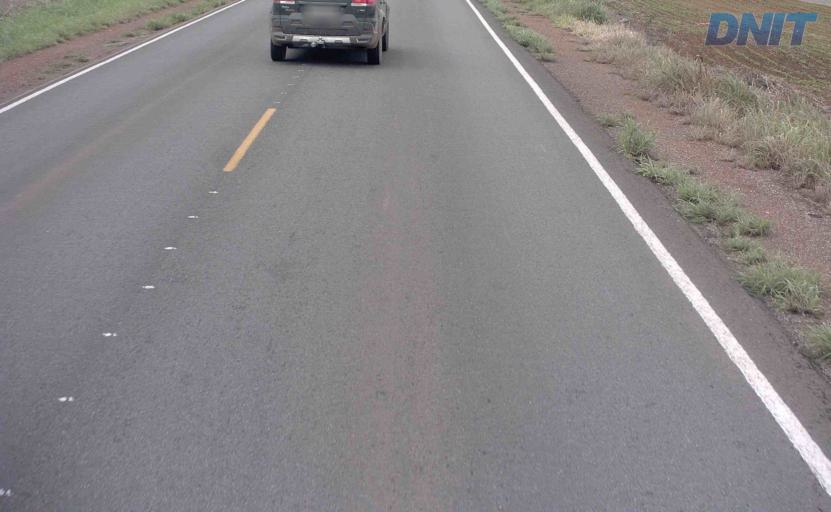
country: BR
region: Goias
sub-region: Padre Bernardo
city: Padre Bernardo
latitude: -15.3241
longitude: -48.2306
